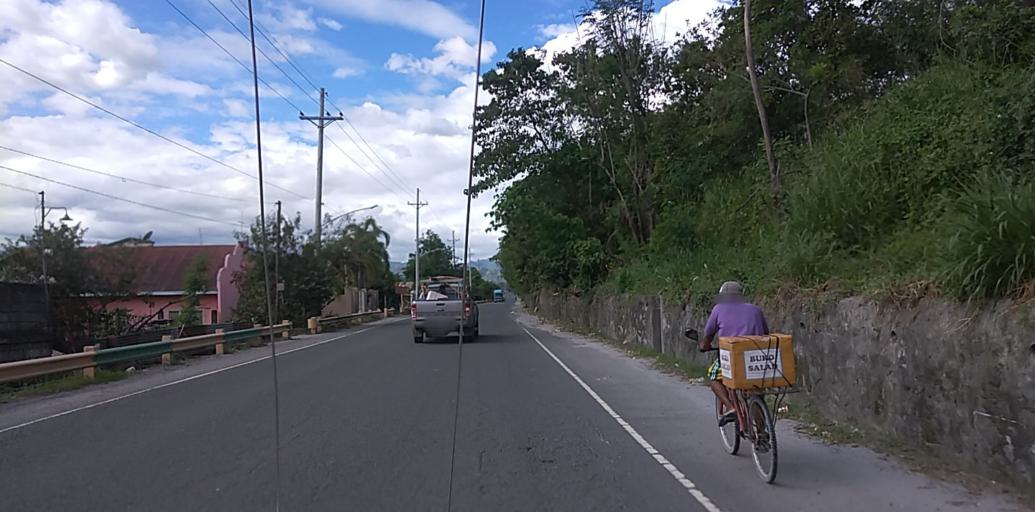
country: PH
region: Central Luzon
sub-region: Province of Pampanga
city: Dolores
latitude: 15.0928
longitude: 120.5333
